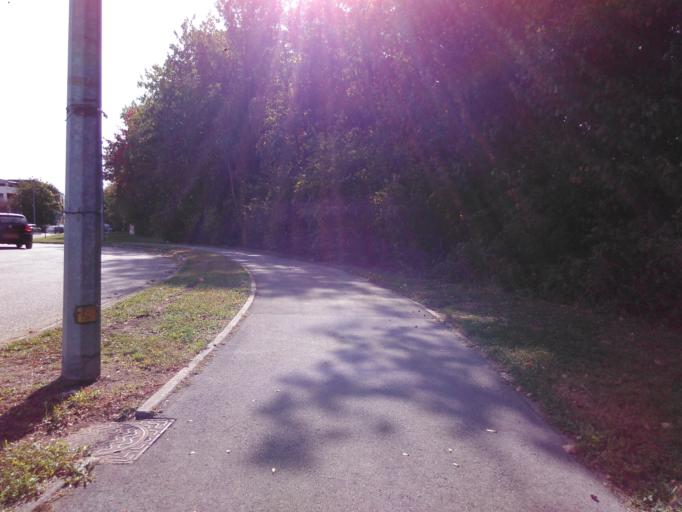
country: FR
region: Lorraine
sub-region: Departement de la Moselle
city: Thionville
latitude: 49.3787
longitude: 6.1693
